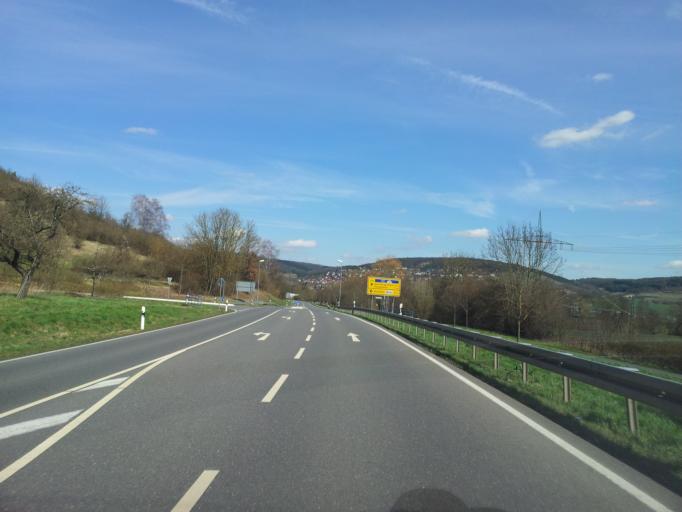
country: DE
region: Baden-Wuerttemberg
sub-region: Regierungsbezirk Stuttgart
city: Lauda-Konigshofen
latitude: 49.5359
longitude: 9.7175
